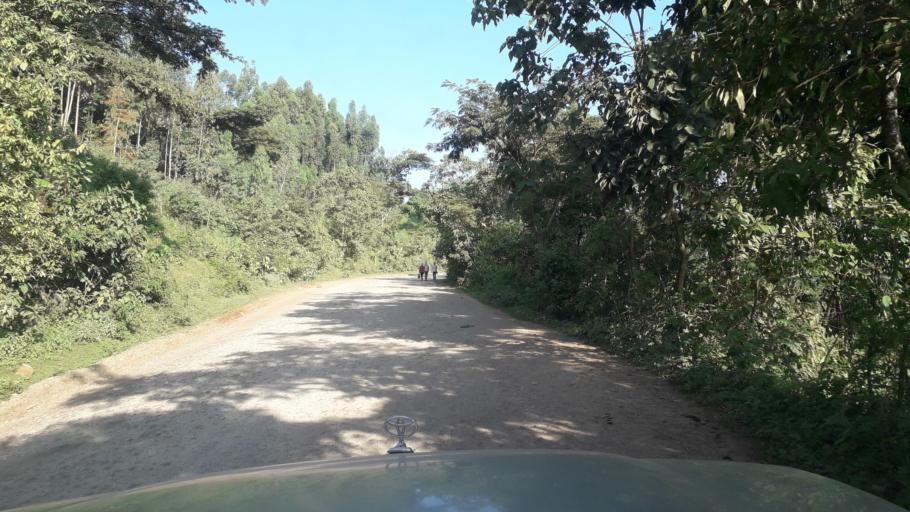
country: ET
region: Oromiya
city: Jima
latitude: 7.4855
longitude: 36.8766
